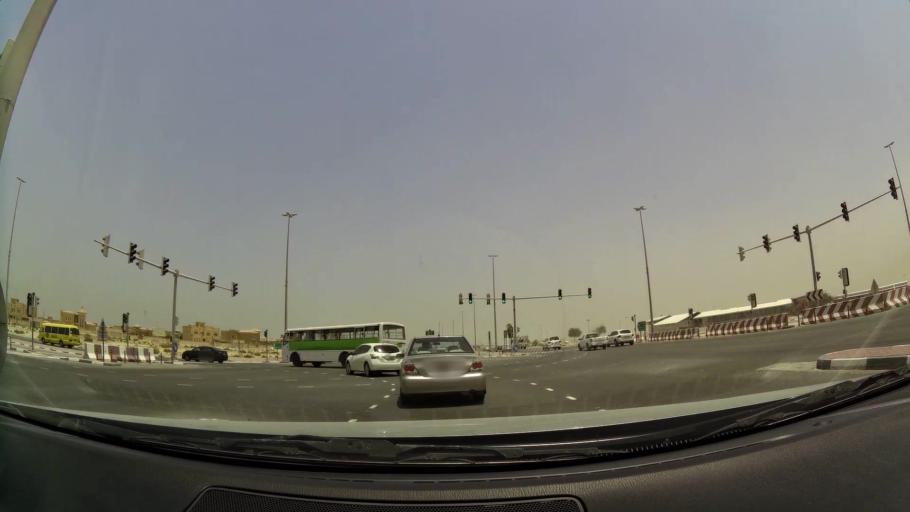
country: AE
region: Dubai
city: Dubai
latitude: 25.0812
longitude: 55.2499
